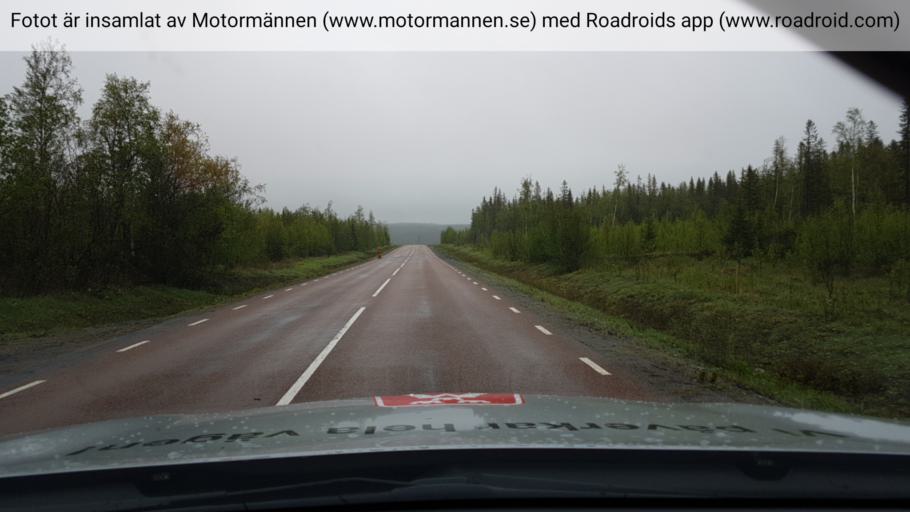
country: SE
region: Jaemtland
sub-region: Krokoms Kommun
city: Valla
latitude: 63.1428
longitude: 13.9444
